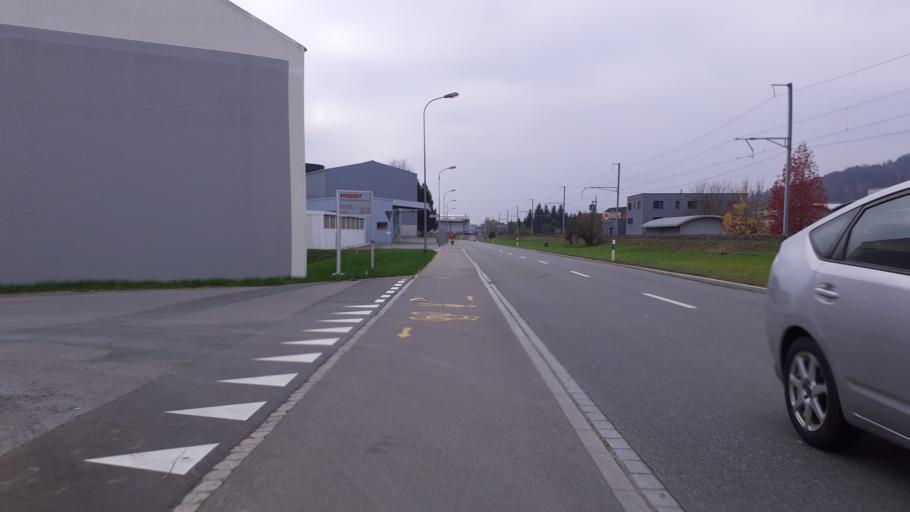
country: CH
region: Saint Gallen
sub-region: Wahlkreis Rheintal
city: Au
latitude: 47.4232
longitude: 9.6383
